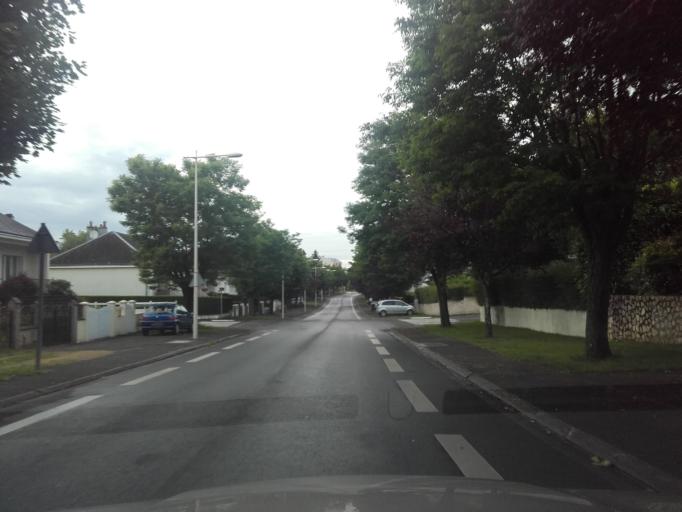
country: FR
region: Centre
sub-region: Departement d'Indre-et-Loire
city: Joue-les-Tours
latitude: 47.3466
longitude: 0.6811
